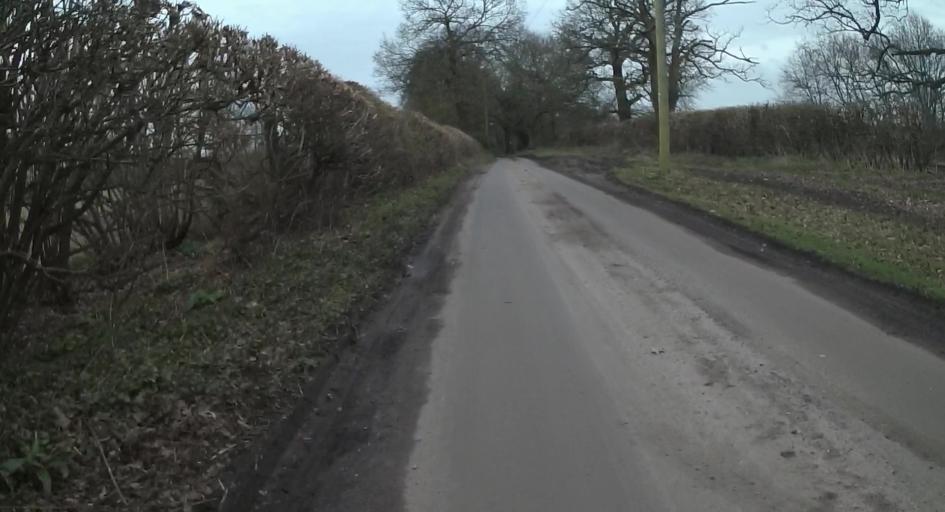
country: GB
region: England
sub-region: Hampshire
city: Overton
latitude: 51.2564
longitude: -1.1983
